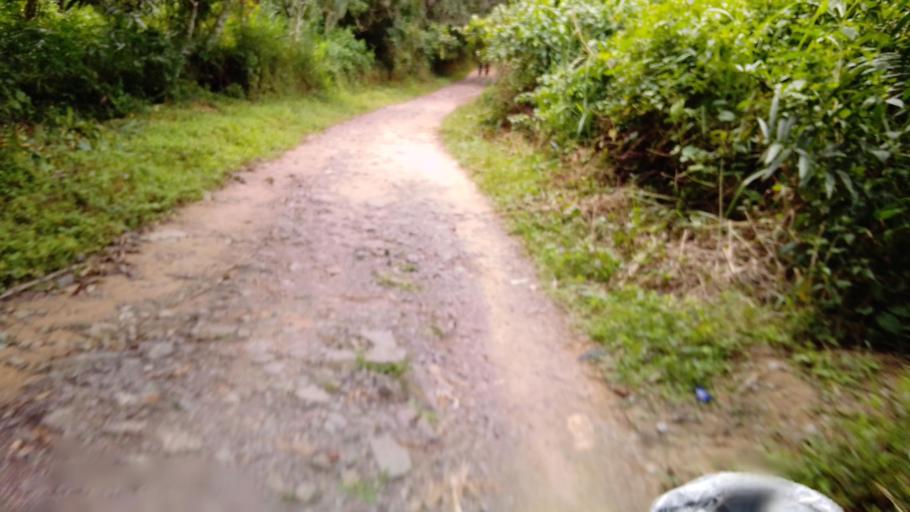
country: SL
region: Eastern Province
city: Koidu
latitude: 8.6596
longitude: -10.9365
